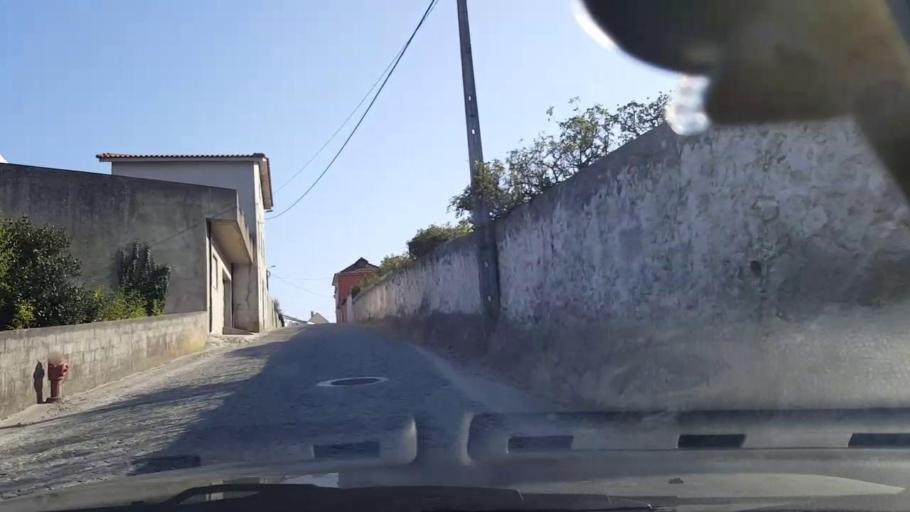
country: PT
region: Porto
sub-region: Vila do Conde
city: Arvore
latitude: 41.3554
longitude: -8.7220
